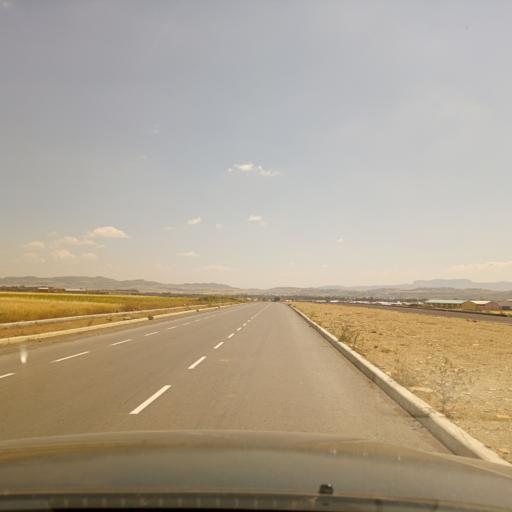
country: ET
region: Tigray
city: Mekele
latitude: 13.4838
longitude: 39.4255
